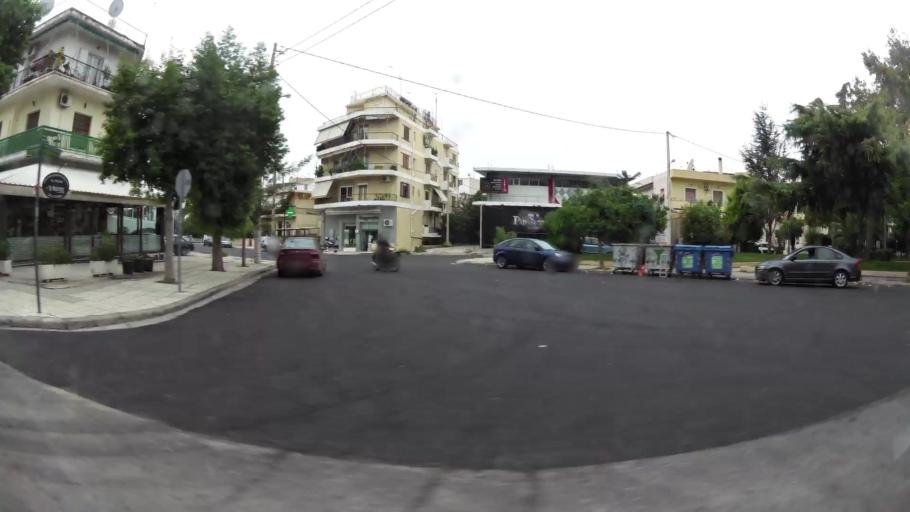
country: GR
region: Attica
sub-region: Nomarchia Athinas
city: Peristeri
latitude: 38.0084
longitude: 23.7066
